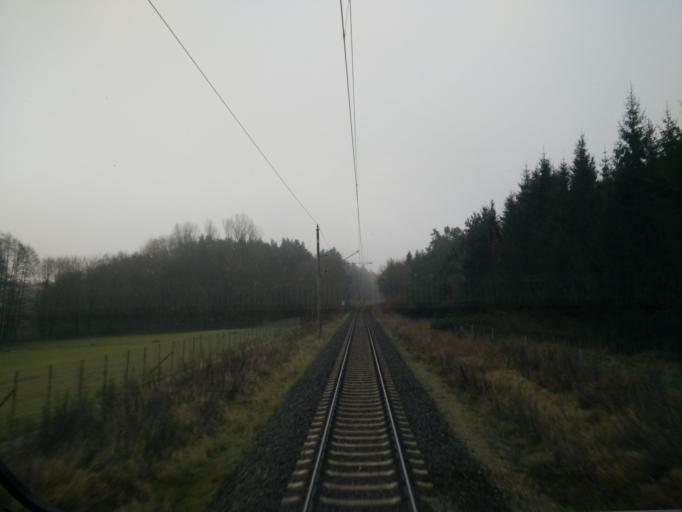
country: DE
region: Mecklenburg-Vorpommern
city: Bad Kleinen
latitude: 53.7915
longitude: 11.4868
